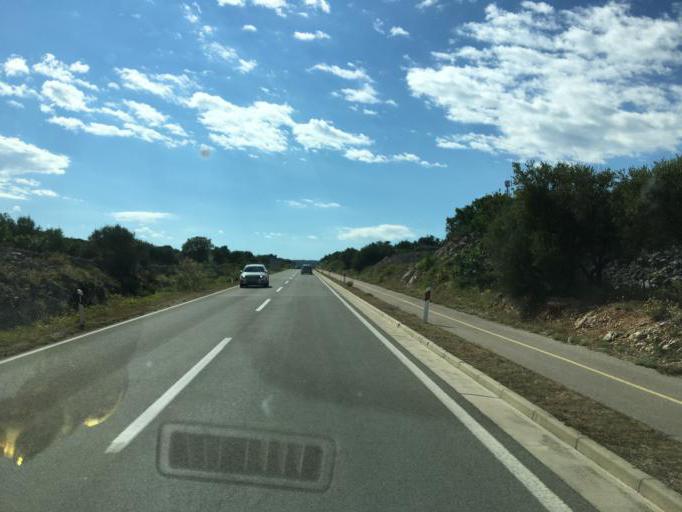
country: HR
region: Primorsko-Goranska
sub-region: Grad Krk
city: Krk
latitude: 45.0331
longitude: 14.5841
